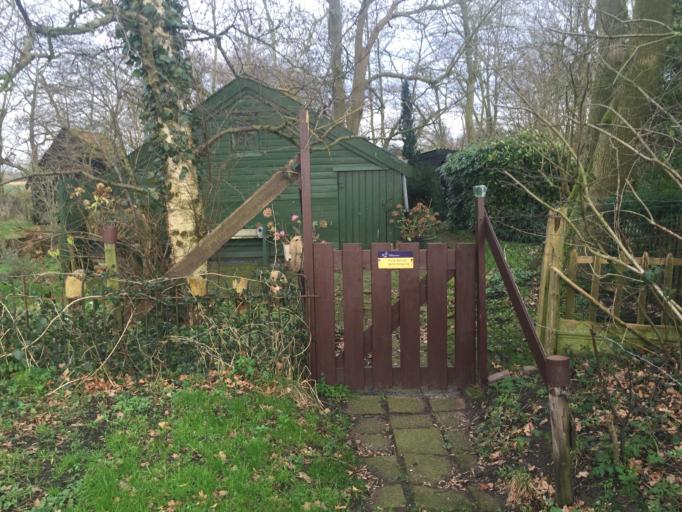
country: NL
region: North Holland
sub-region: Gemeente Bussum
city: Bussum
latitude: 52.2850
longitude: 5.1405
